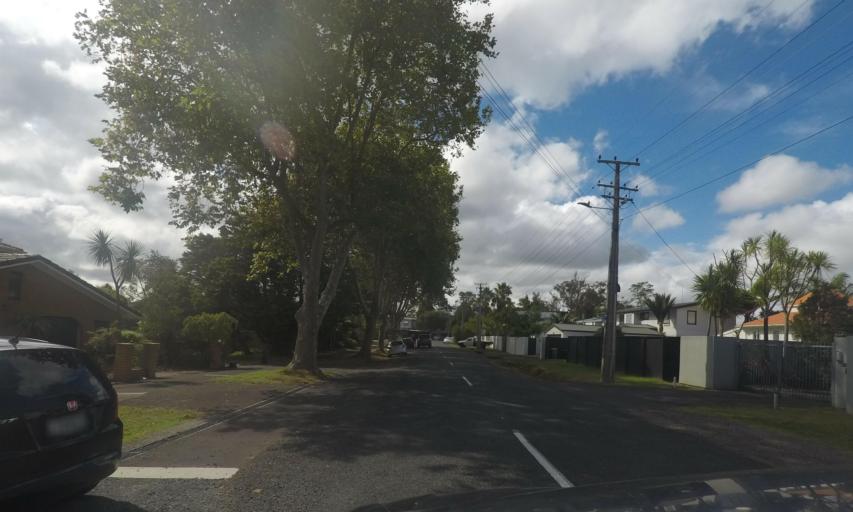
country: NZ
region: Auckland
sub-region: Auckland
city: North Shore
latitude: -36.7781
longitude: 174.6608
